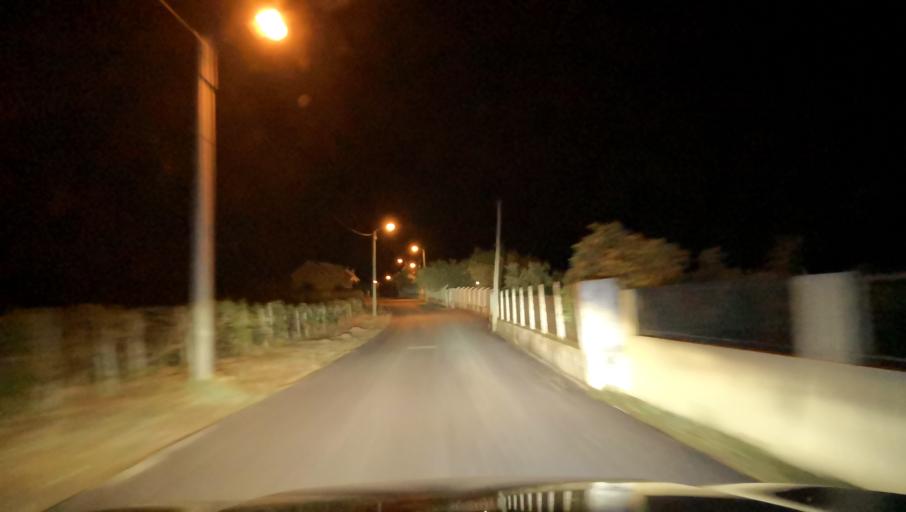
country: PT
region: Vila Real
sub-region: Sabrosa
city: Vilela
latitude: 41.2100
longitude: -7.6950
